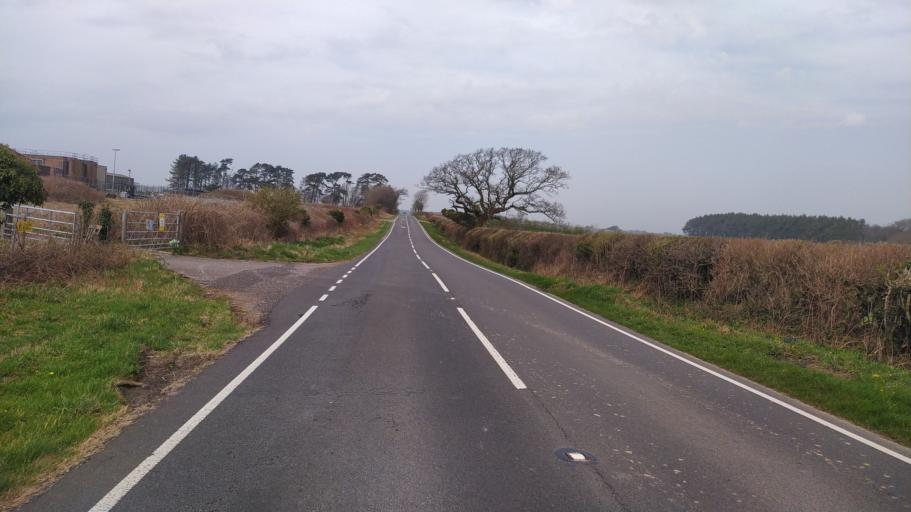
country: GB
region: England
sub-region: Dorset
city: Beaminster
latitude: 50.8091
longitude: -2.6408
